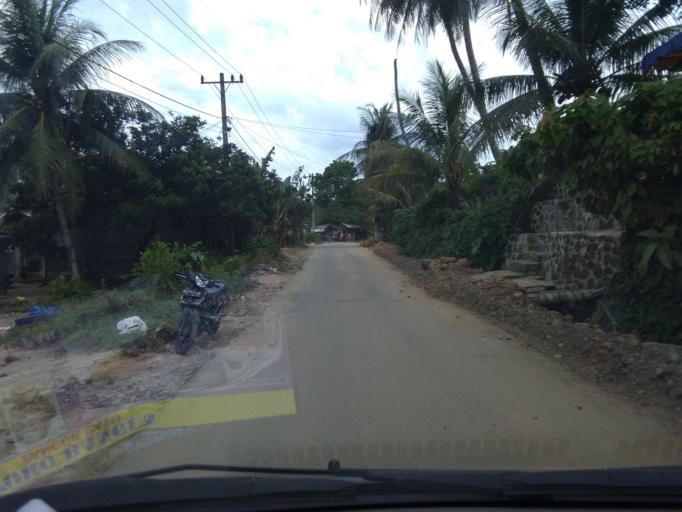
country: ID
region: North Sumatra
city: Deli Tua
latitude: 3.3070
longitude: 98.8106
